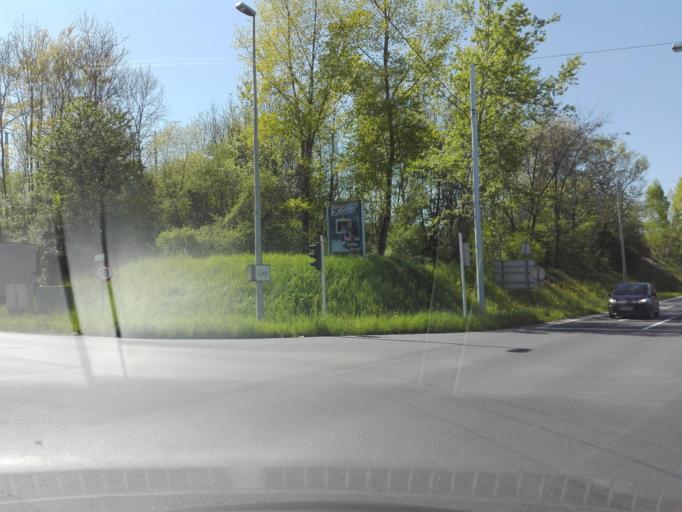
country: AT
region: Upper Austria
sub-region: Politischer Bezirk Urfahr-Umgebung
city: Steyregg
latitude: 48.2578
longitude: 14.3304
